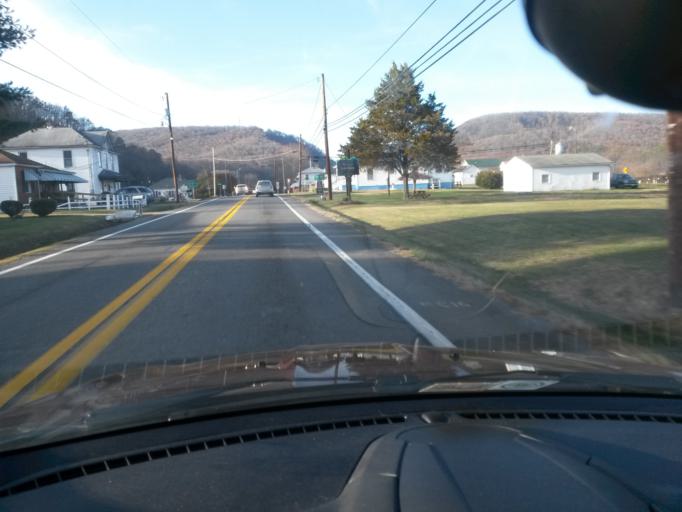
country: US
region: Virginia
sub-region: Alleghany County
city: Clifton Forge
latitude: 37.7924
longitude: -79.7862
